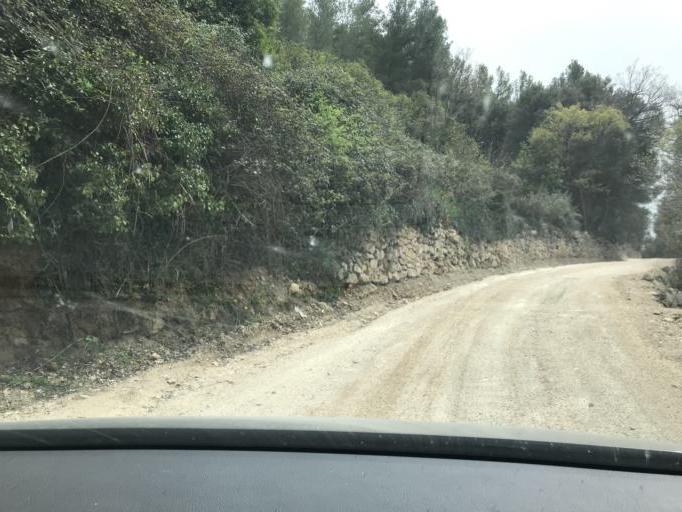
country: ES
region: Andalusia
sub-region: Provincia de Granada
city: Castril
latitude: 37.8379
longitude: -2.7730
